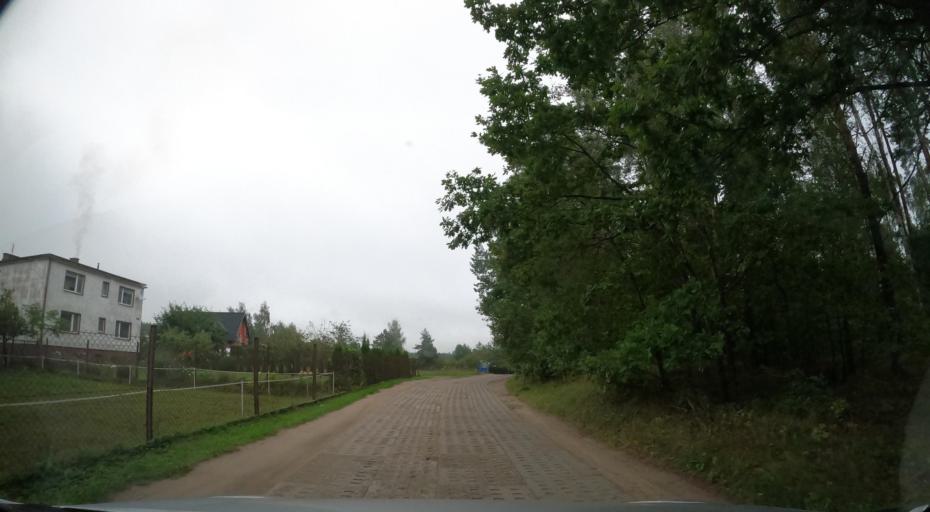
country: PL
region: Pomeranian Voivodeship
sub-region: Powiat kartuski
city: Chwaszczyno
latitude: 54.4218
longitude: 18.4173
